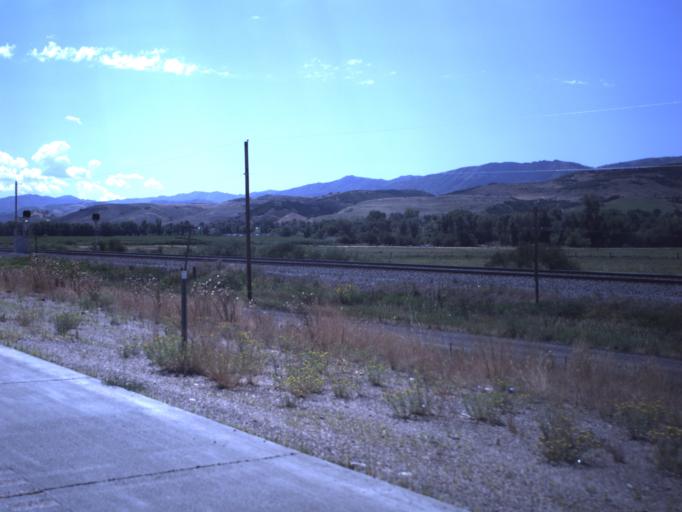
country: US
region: Utah
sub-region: Morgan County
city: Mountain Green
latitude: 41.1007
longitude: -111.7437
